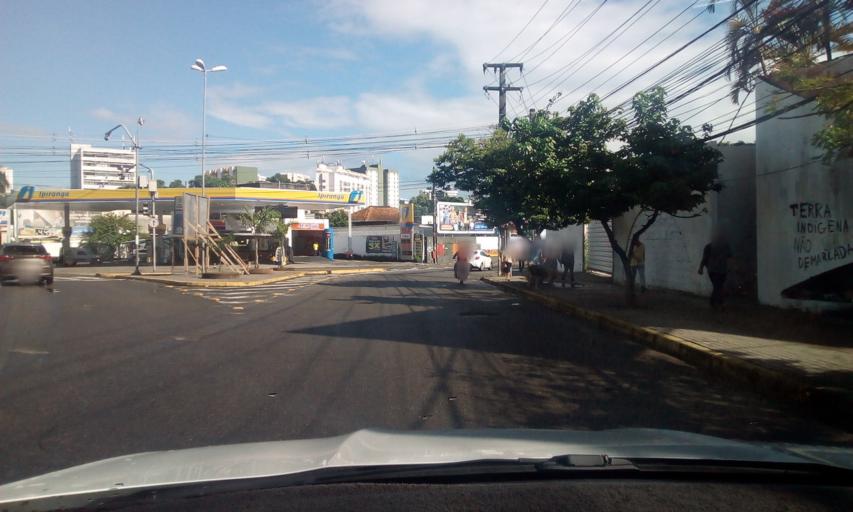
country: BR
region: Pernambuco
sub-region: Recife
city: Recife
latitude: -8.0559
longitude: -34.8949
